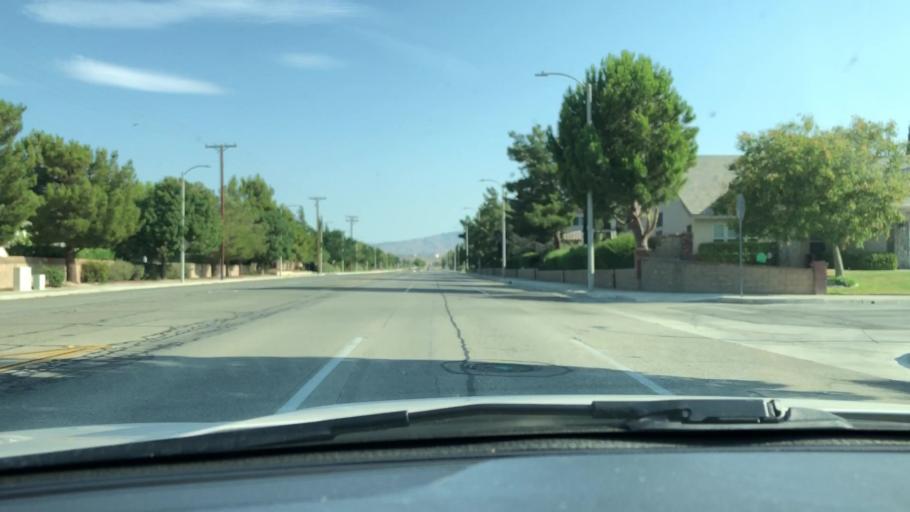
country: US
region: California
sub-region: Los Angeles County
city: Quartz Hill
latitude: 34.6872
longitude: -118.2016
